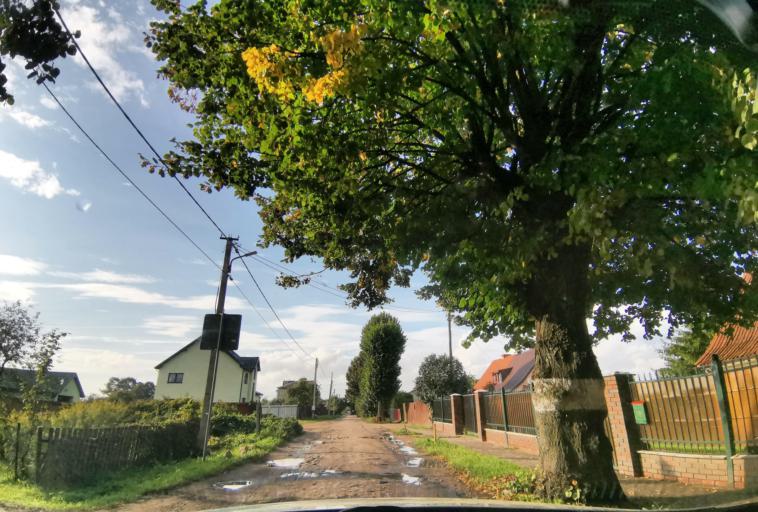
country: RU
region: Kaliningrad
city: Chernyakhovsk
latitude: 54.6561
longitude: 21.8380
